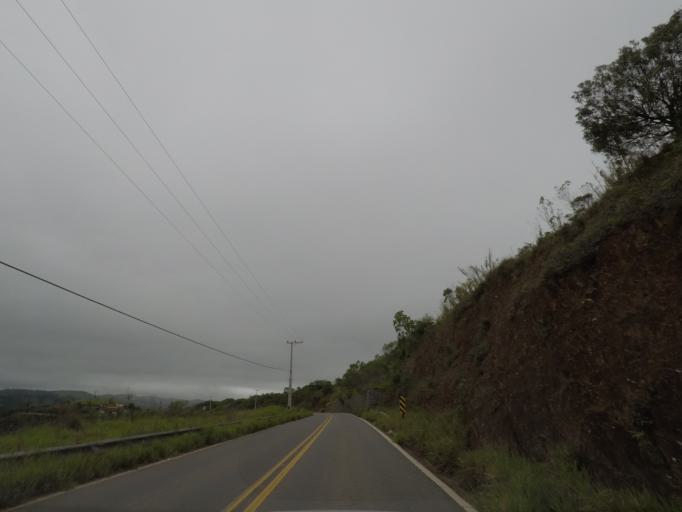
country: BR
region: Sao Paulo
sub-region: Cunha
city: Cunha
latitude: -23.0901
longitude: -44.9602
